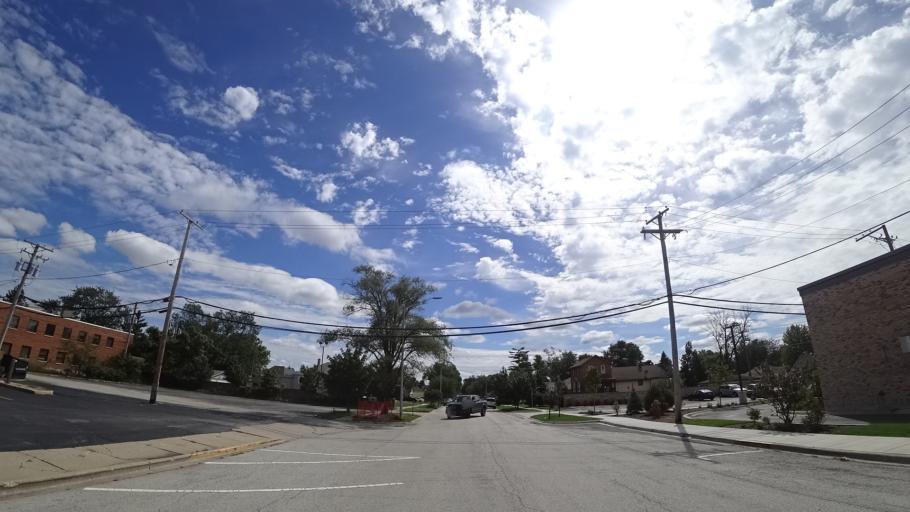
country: US
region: Illinois
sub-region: Cook County
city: Burbank
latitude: 41.7193
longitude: -87.7763
